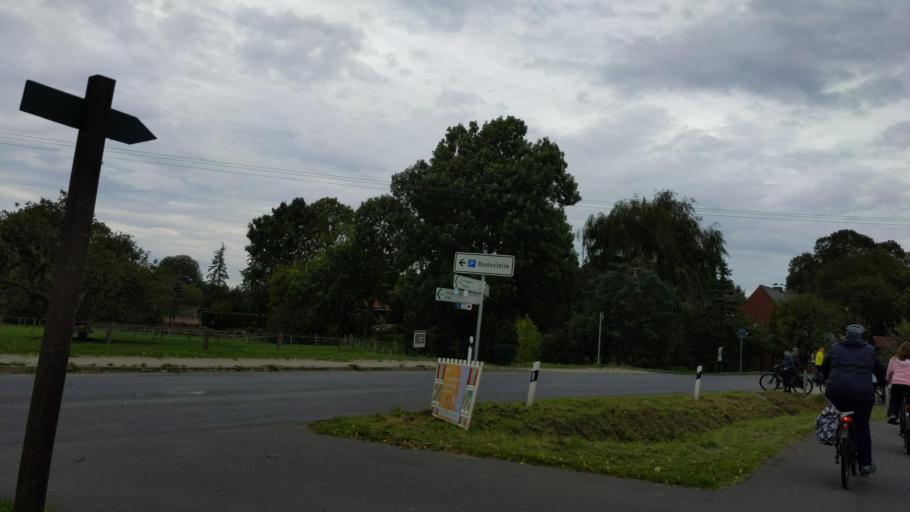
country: DE
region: Schleswig-Holstein
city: Gross Sarau
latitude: 53.7668
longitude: 10.7700
